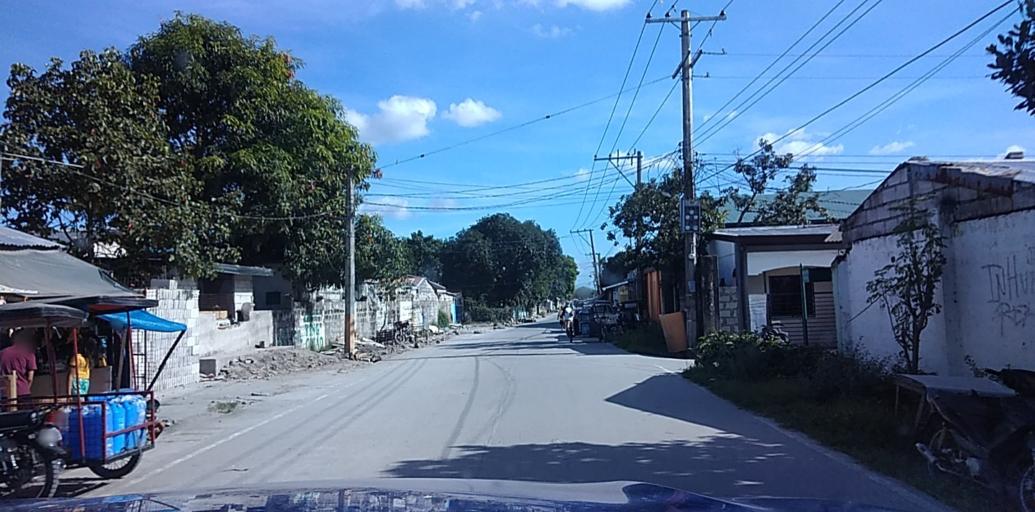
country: PH
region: Central Luzon
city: Santol
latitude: 15.1497
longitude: 120.5453
